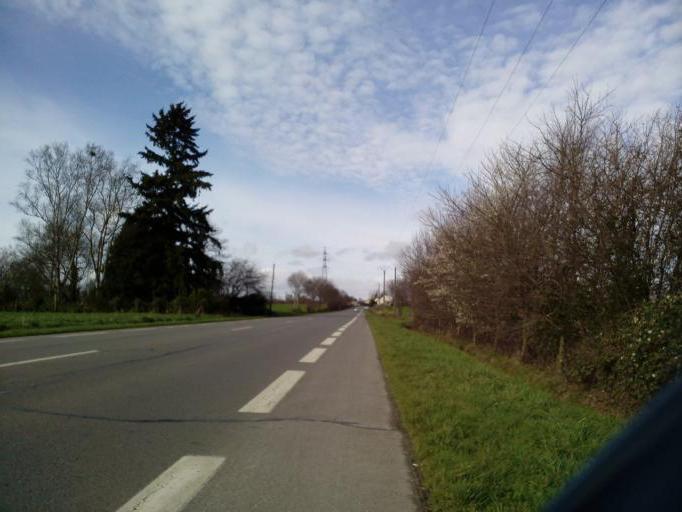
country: FR
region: Brittany
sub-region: Departement d'Ille-et-Vilaine
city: Montgermont
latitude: 48.1648
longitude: -1.7147
